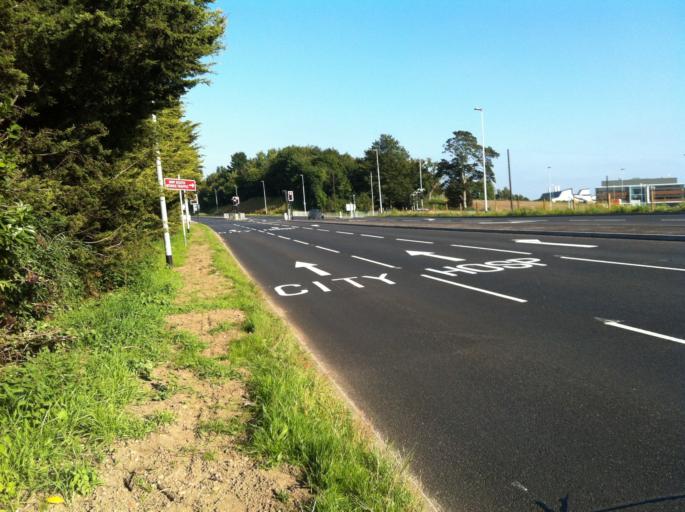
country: GB
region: England
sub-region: Norfolk
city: Bowthorpe
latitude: 52.6242
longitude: 1.2150
